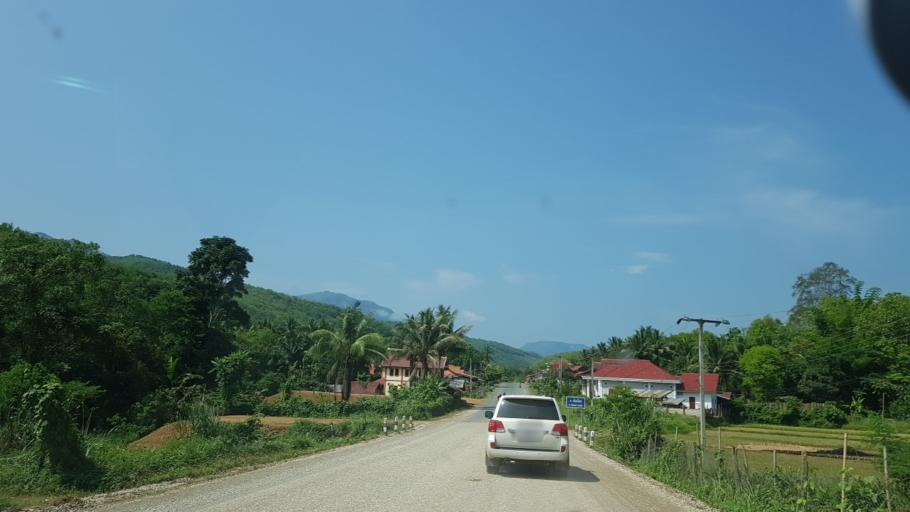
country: LA
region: Louangphabang
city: Xiang Ngeun
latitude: 19.7329
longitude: 102.1555
